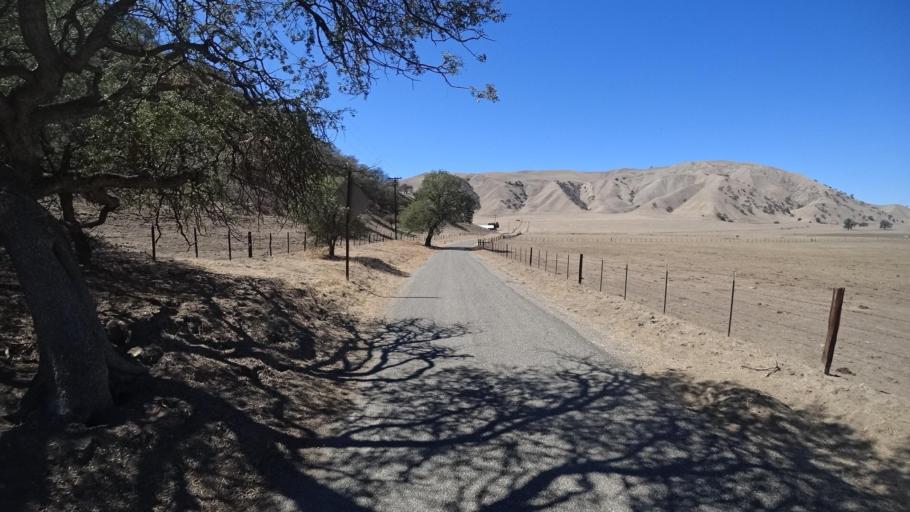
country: US
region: California
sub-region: Monterey County
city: King City
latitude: 36.3100
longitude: -120.9218
